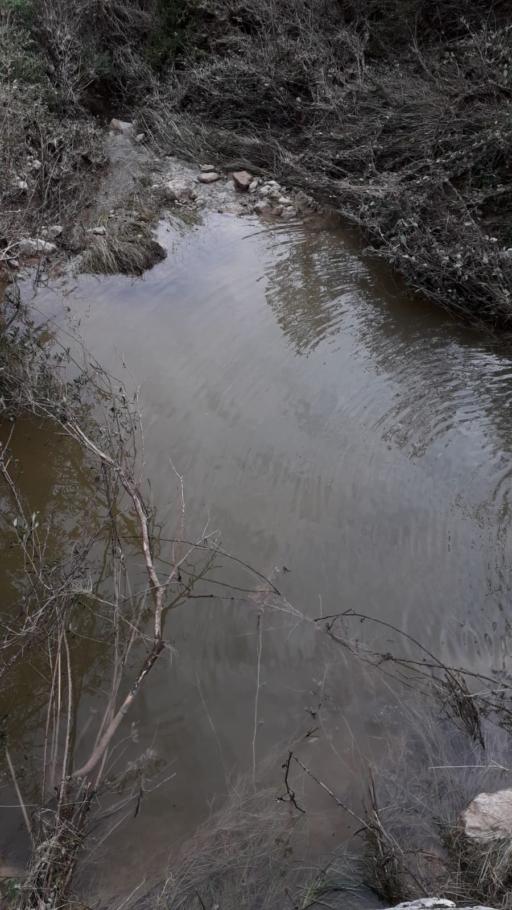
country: ES
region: Catalonia
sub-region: Provincia de Barcelona
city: Bellprat
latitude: 41.5032
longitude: 1.4216
